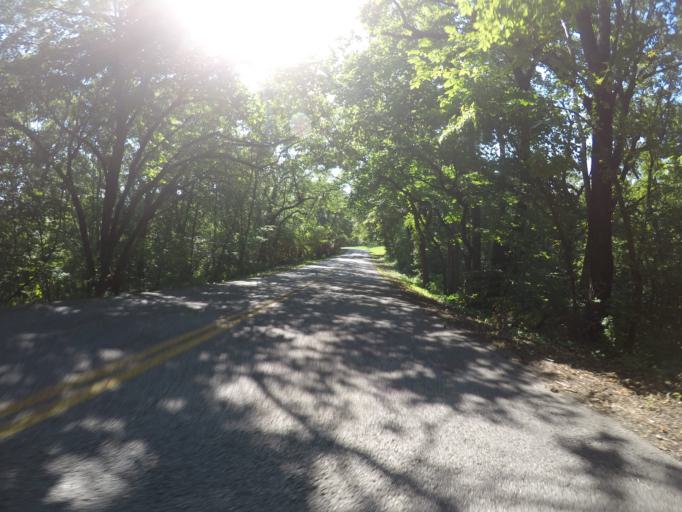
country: US
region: Missouri
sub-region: Platte County
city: Parkville
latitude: 39.1628
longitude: -94.7670
